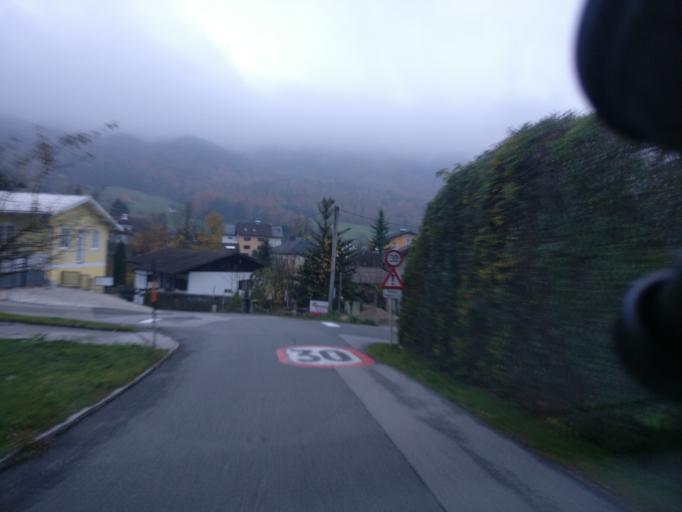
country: AT
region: Salzburg
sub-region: Politischer Bezirk Salzburg-Umgebung
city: Hallwang
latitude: 47.8455
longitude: 13.0977
